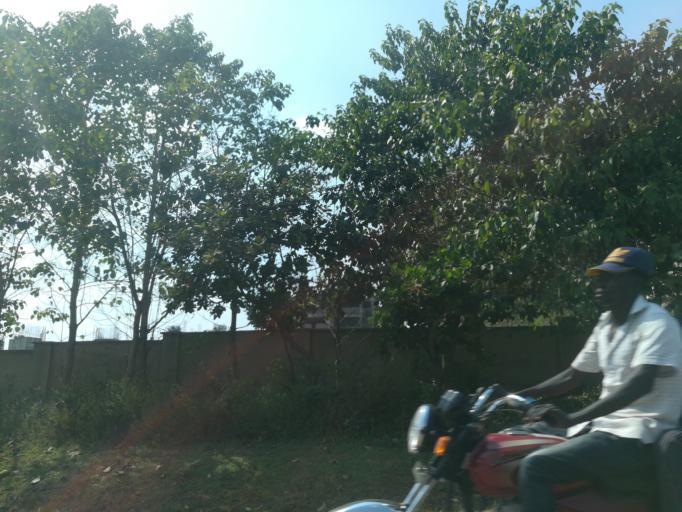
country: NG
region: Abuja Federal Capital Territory
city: Abuja
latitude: 9.0621
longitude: 7.4300
